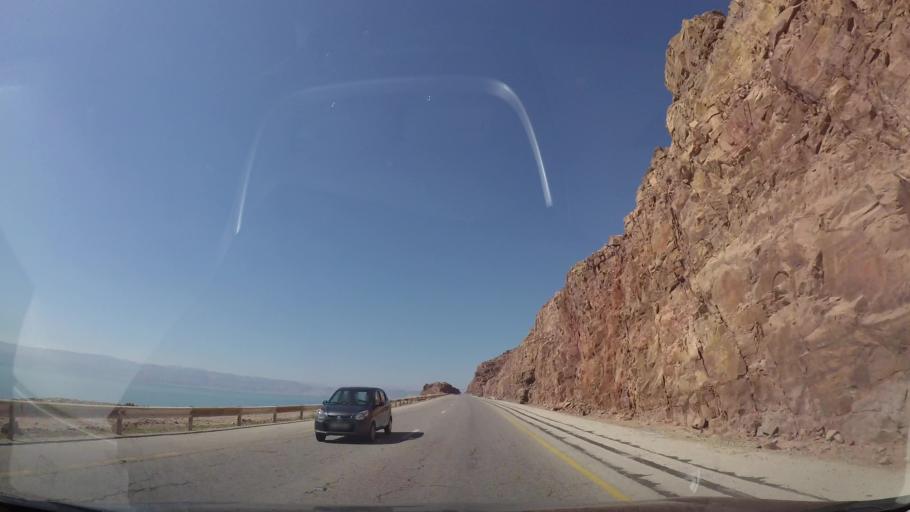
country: JO
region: Karak
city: Al Qasr
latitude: 31.4876
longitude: 35.5705
